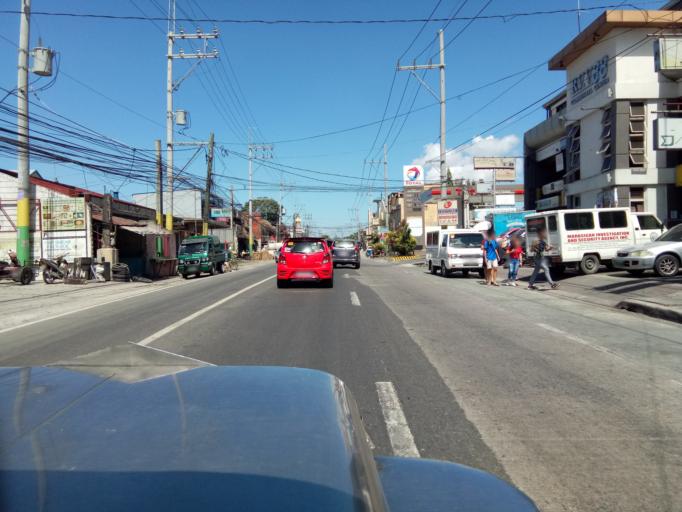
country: PH
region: Calabarzon
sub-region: Province of Cavite
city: Dasmarinas
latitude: 14.3505
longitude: 120.9395
